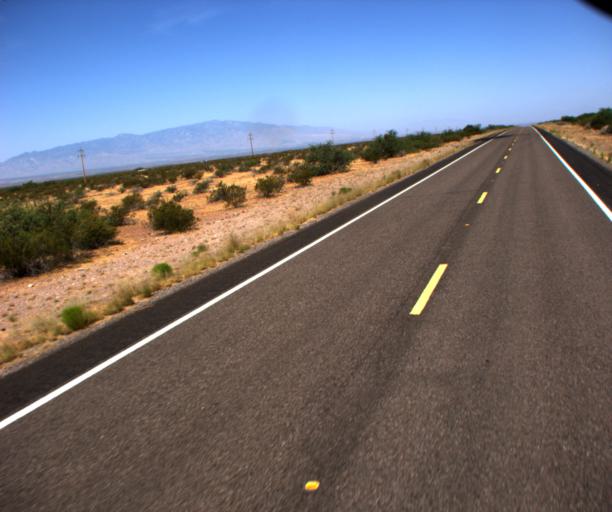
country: US
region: Arizona
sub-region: Graham County
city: Swift Trail Junction
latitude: 32.7580
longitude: -109.4312
